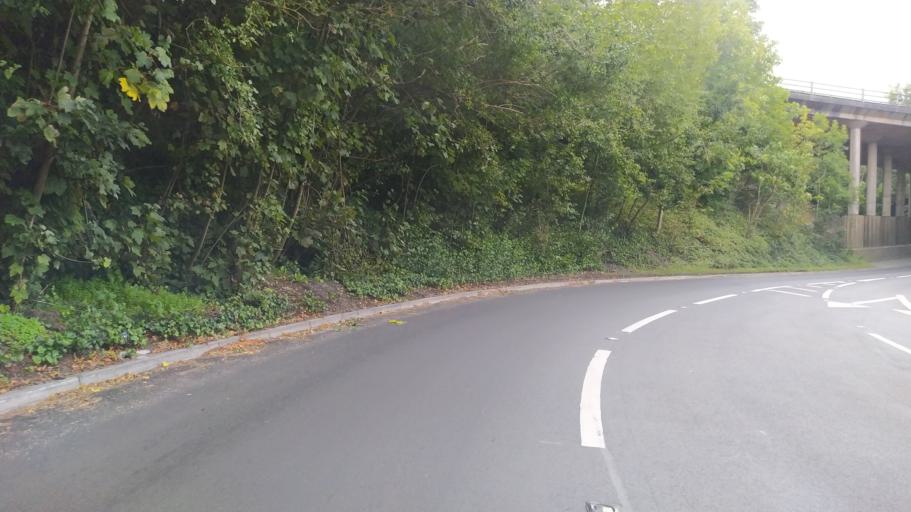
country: GB
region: England
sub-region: Dorset
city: Shaftesbury
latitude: 51.0102
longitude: -2.1970
